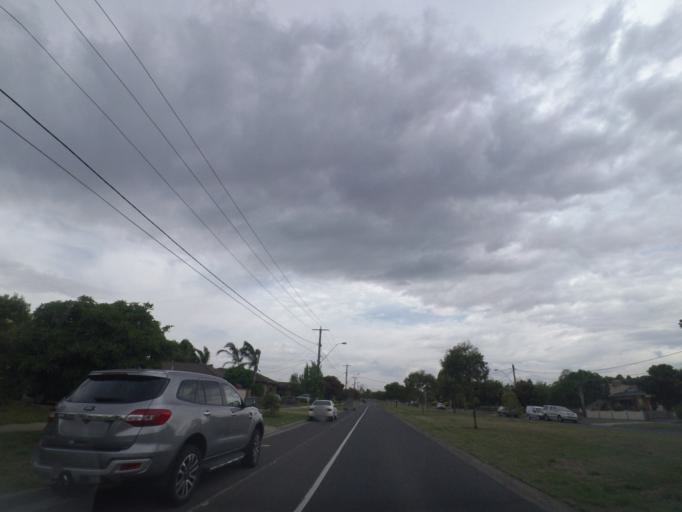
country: AU
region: Victoria
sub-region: Whittlesea
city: Epping
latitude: -37.6424
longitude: 145.0574
